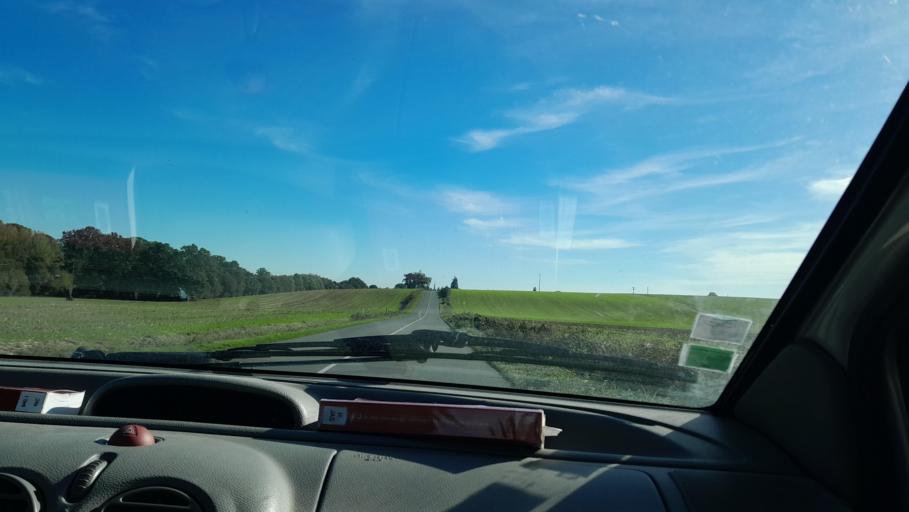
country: FR
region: Brittany
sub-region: Departement d'Ille-et-Vilaine
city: Argentre-du-Plessis
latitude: 48.0005
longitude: -1.1286
